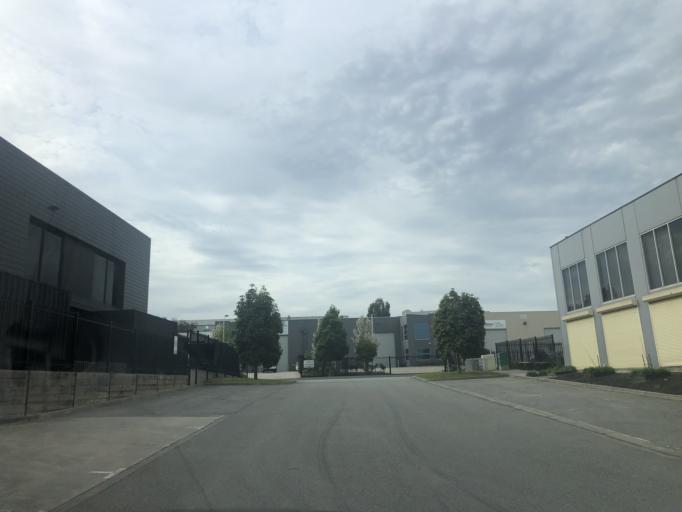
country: AU
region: Victoria
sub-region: Casey
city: Hallam
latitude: -38.0160
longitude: 145.2606
